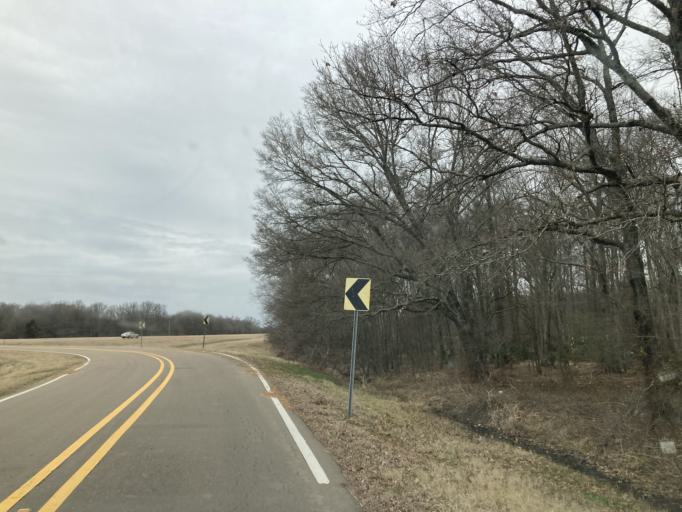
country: US
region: Mississippi
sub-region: Yazoo County
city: Yazoo City
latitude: 33.0035
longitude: -90.4689
